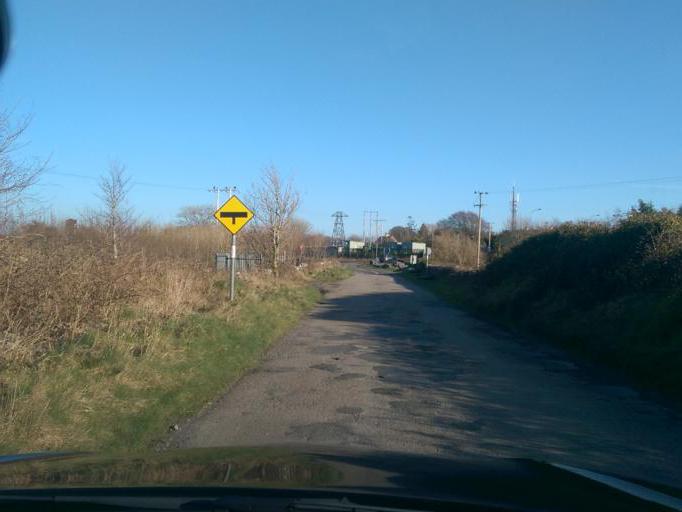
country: IE
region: Connaught
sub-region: County Galway
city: Oranmore
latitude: 53.2126
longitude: -8.8721
